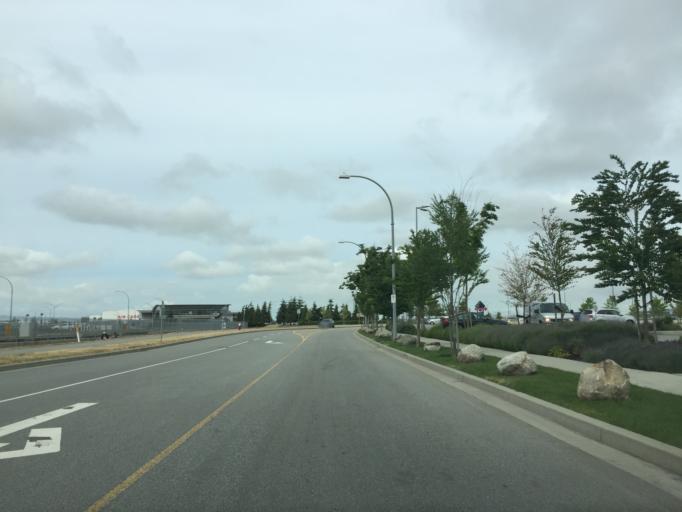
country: CA
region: British Columbia
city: Richmond
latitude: 49.1968
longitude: -123.1421
